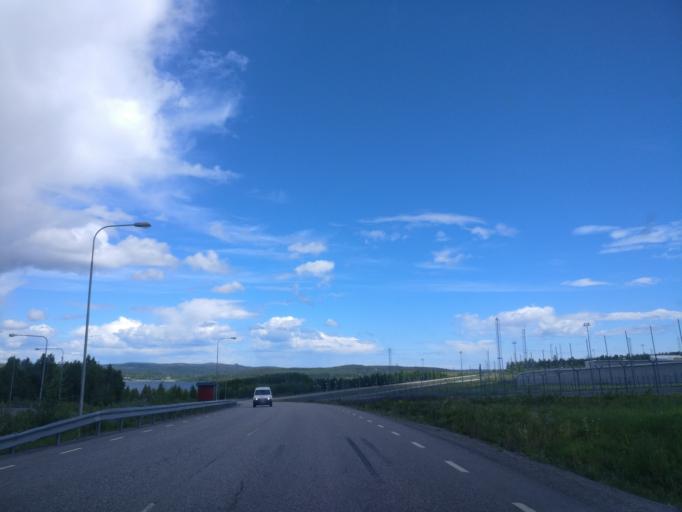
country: SE
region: Vaesternorrland
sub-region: Haernoesands Kommun
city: Haernoesand
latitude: 62.6551
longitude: 17.8916
